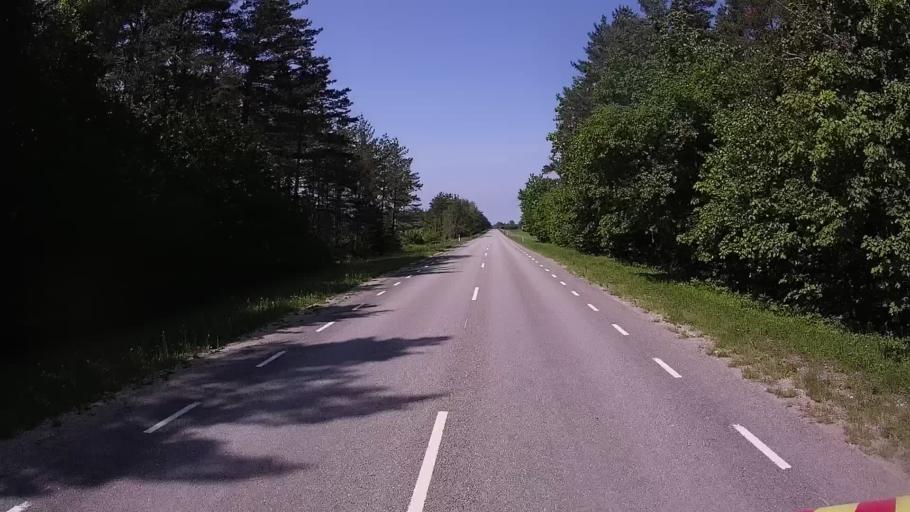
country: EE
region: Saare
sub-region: Kuressaare linn
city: Kuressaare
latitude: 58.3568
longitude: 22.0669
